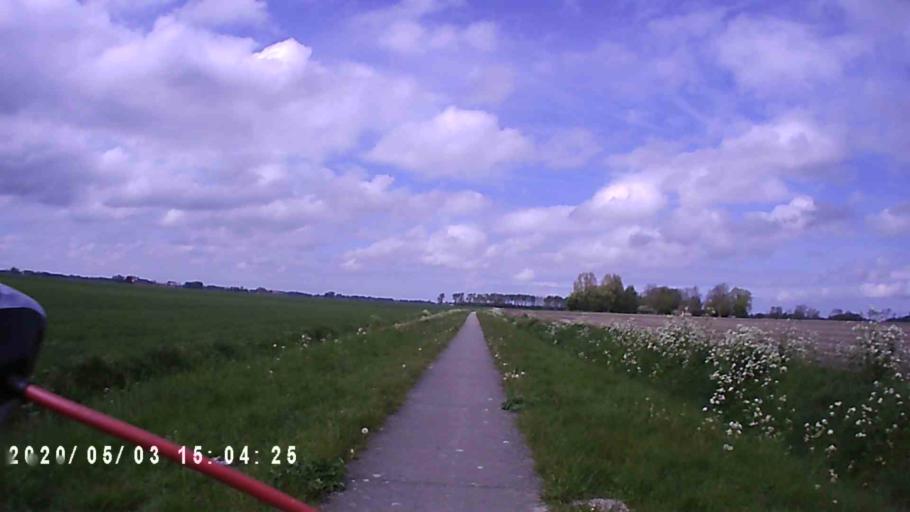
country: NL
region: Groningen
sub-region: Gemeente Zuidhorn
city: Oldehove
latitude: 53.3677
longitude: 6.4427
